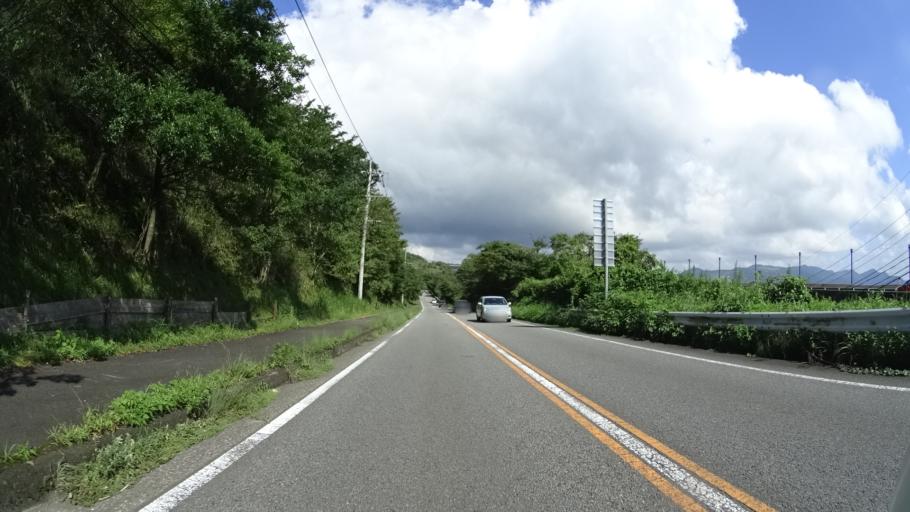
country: JP
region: Oita
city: Beppu
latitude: 33.3384
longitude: 131.4596
